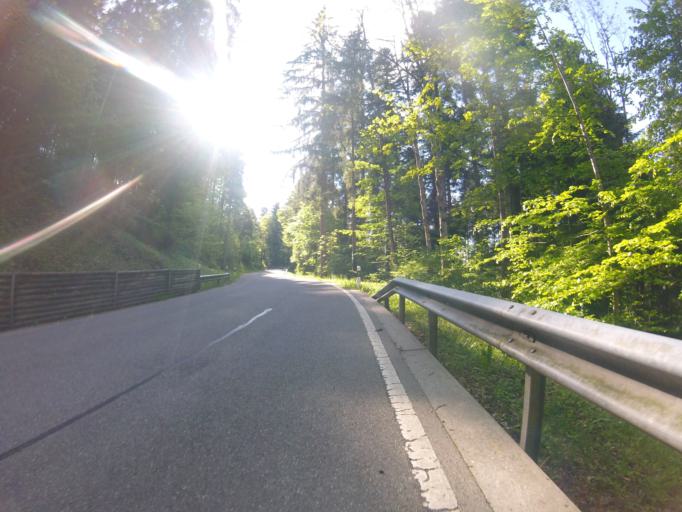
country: CH
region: Saint Gallen
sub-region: Wahlkreis Toggenburg
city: Mogelsberg
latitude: 47.3638
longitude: 9.1474
